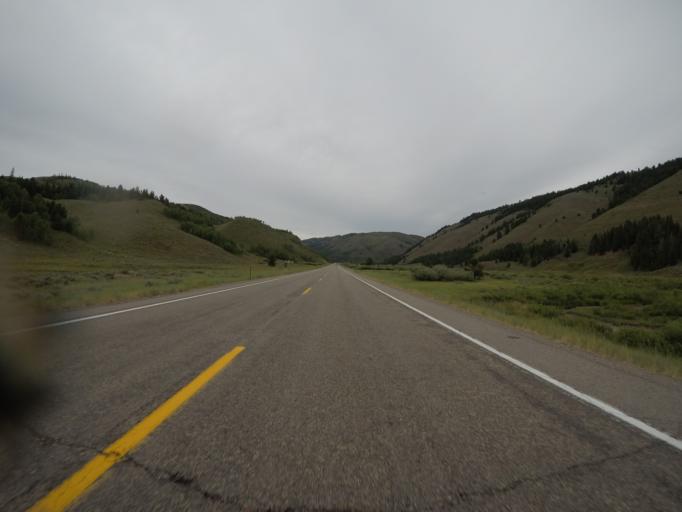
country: US
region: Wyoming
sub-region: Lincoln County
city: Afton
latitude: 42.4723
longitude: -110.9662
